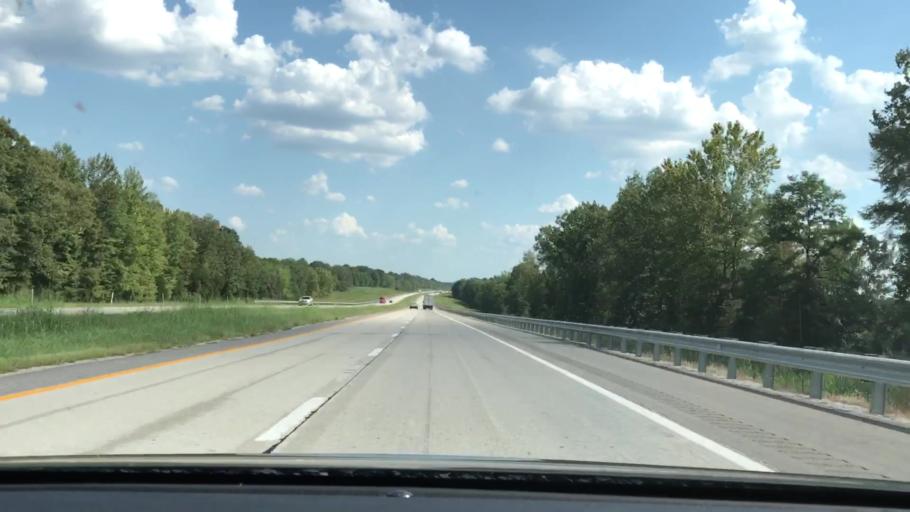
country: US
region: Kentucky
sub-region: Ohio County
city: Oak Grove
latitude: 37.3481
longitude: -86.7810
